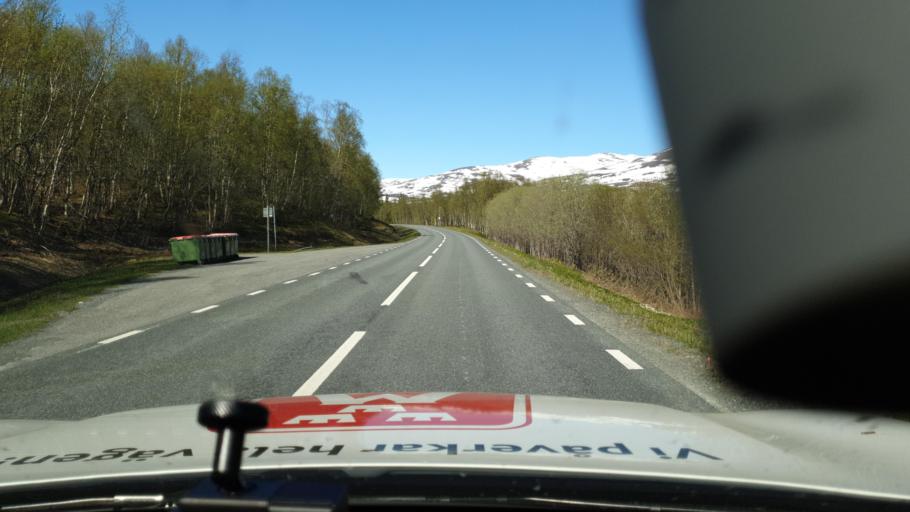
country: NO
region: Nordland
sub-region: Rana
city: Mo i Rana
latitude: 65.7558
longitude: 15.1129
